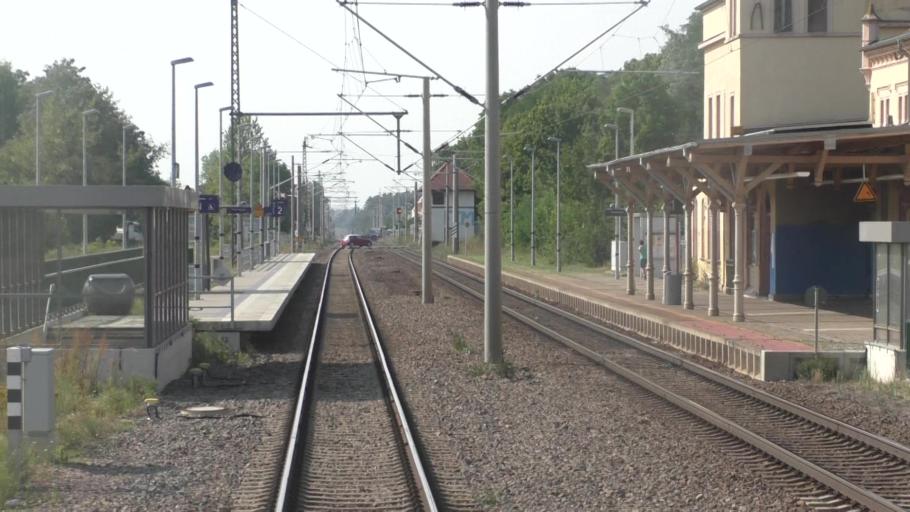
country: DE
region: Saxony-Anhalt
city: Zerbst
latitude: 51.9537
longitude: 12.0897
